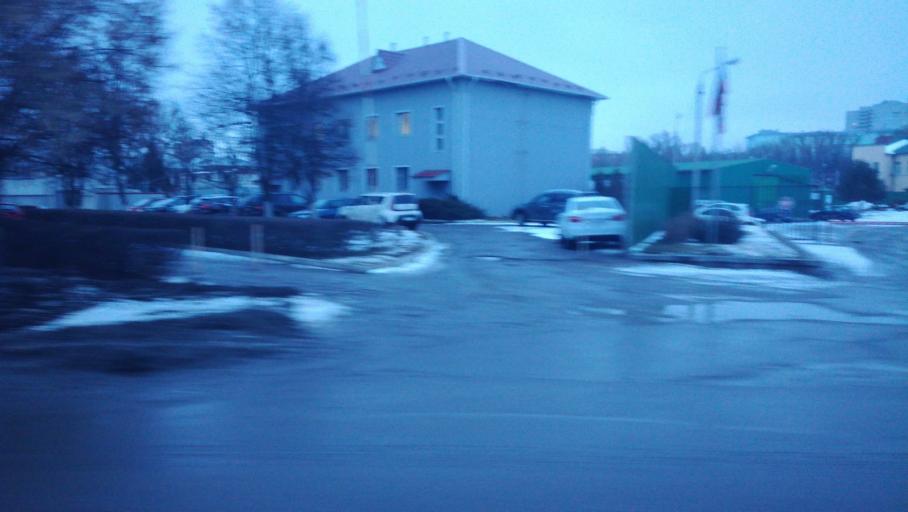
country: RU
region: Tula
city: Tula
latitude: 54.1962
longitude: 37.5768
